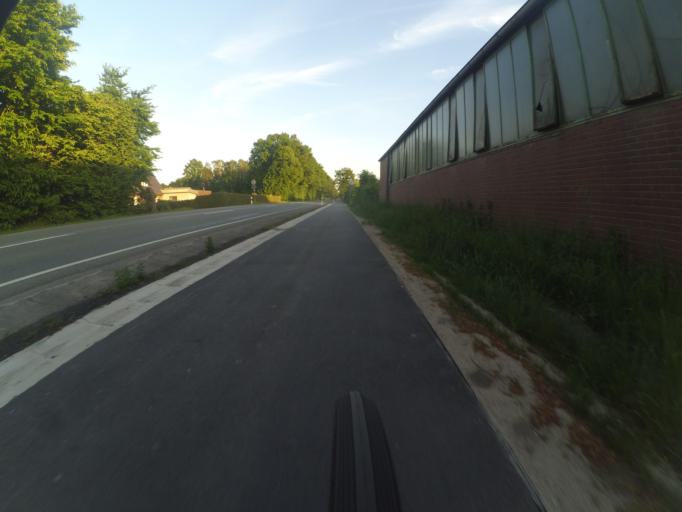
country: DE
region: North Rhine-Westphalia
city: Ibbenburen
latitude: 52.3255
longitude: 7.6688
